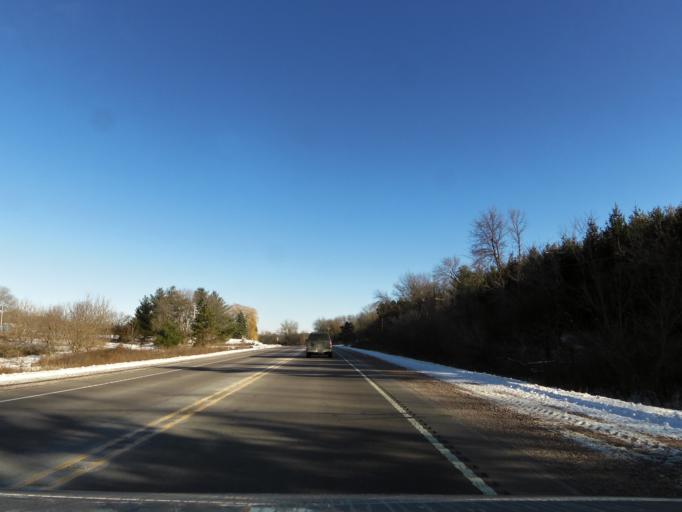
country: US
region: Wisconsin
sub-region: Columbia County
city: Portage
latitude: 43.5077
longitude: -89.5394
